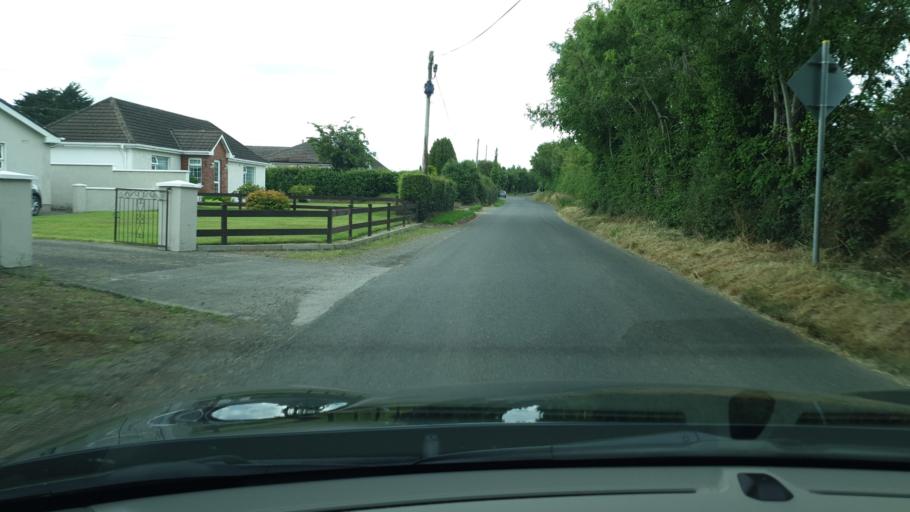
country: IE
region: Leinster
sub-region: An Mhi
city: Ashbourne
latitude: 53.4783
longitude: -6.3751
